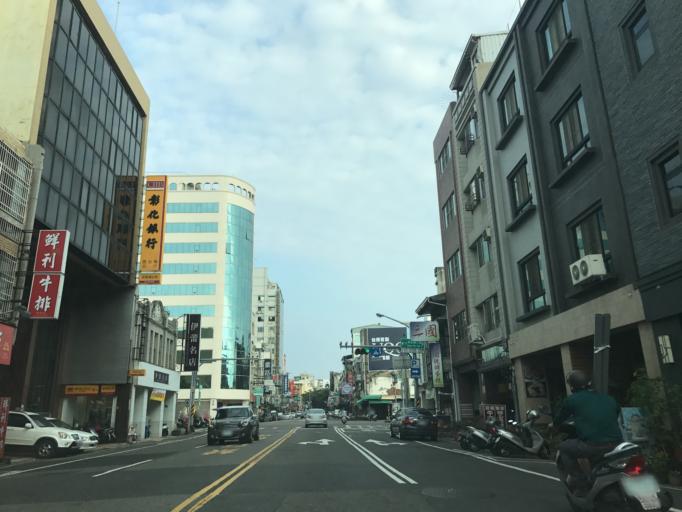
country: TW
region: Taiwan
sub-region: Tainan
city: Tainan
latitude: 22.9984
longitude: 120.1971
